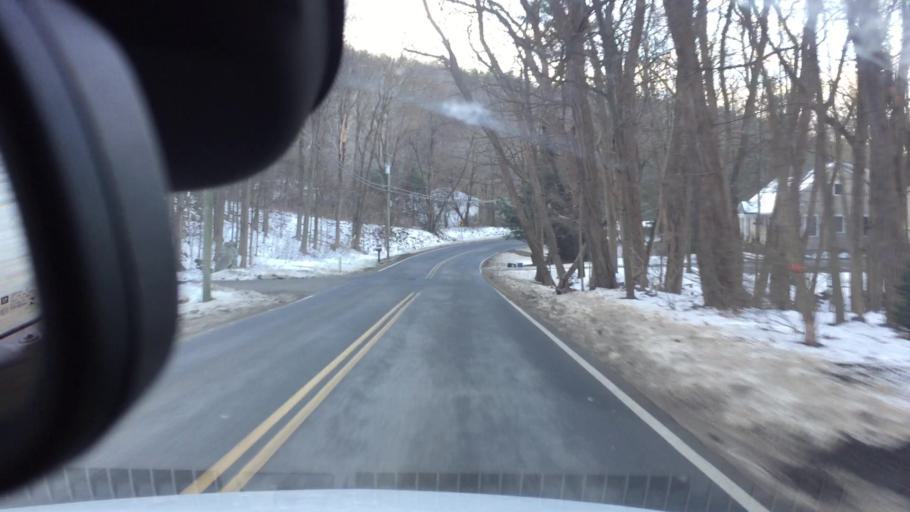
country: US
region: Massachusetts
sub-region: Franklin County
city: Montague
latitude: 42.5033
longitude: -72.5400
